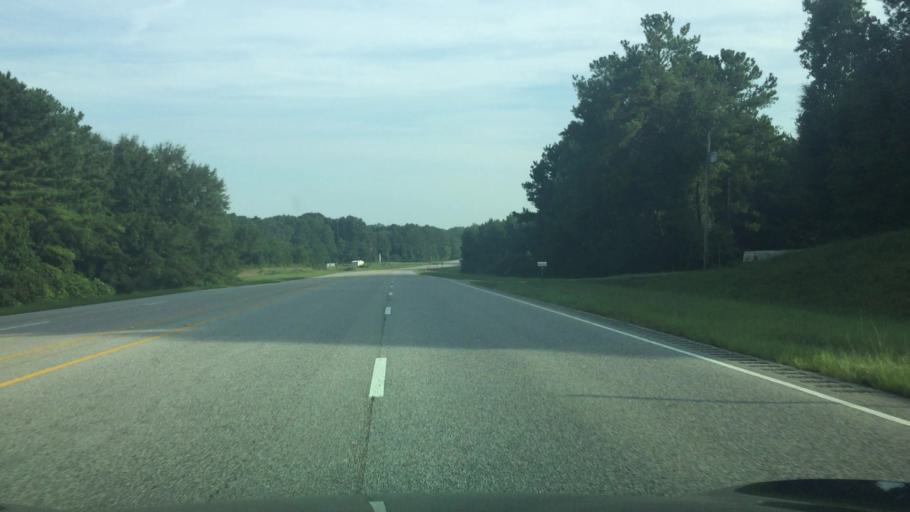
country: US
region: Alabama
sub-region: Covington County
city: Andalusia
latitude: 31.4180
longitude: -86.6093
